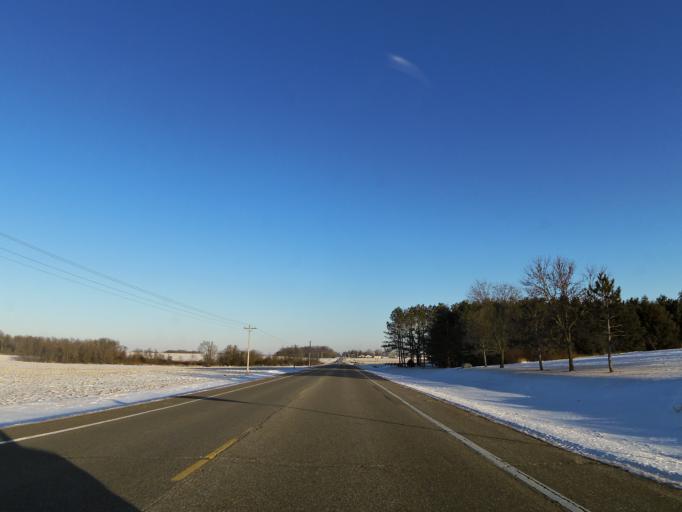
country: US
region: Minnesota
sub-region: Rice County
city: Northfield
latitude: 44.5436
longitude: -93.2134
